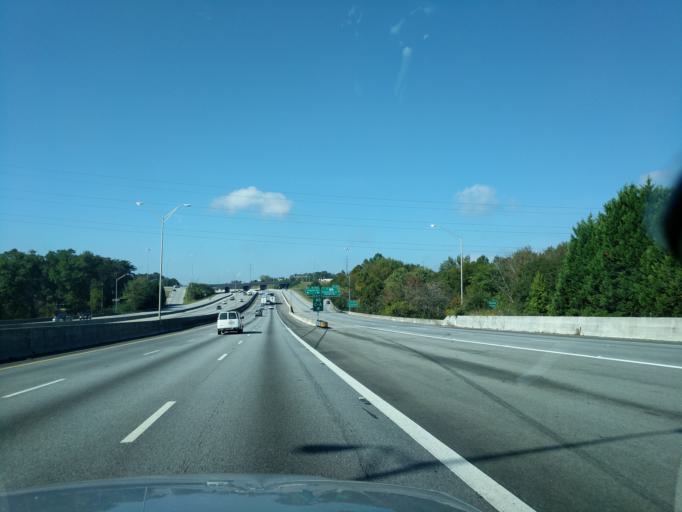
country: US
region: South Carolina
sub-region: Greenville County
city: Mauldin
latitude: 34.8022
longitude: -82.3592
